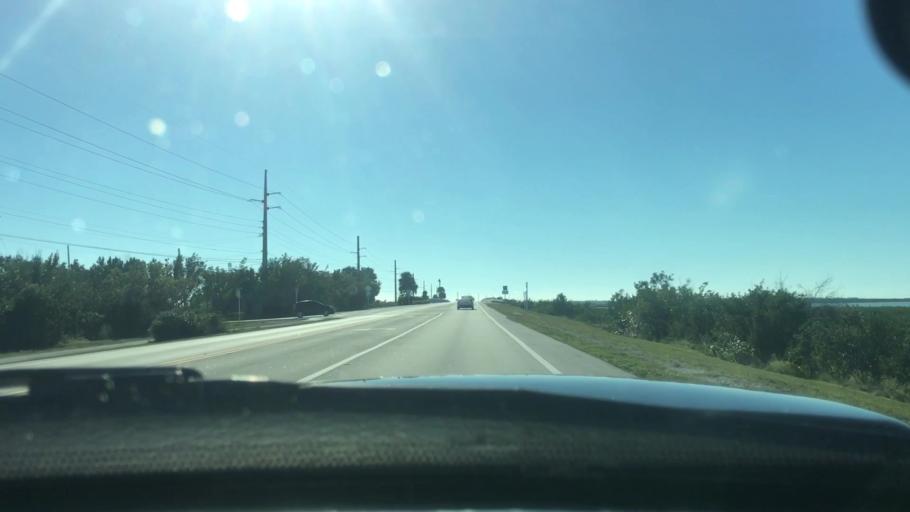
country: US
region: Florida
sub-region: Monroe County
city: Big Coppitt Key
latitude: 24.6248
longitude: -81.6003
